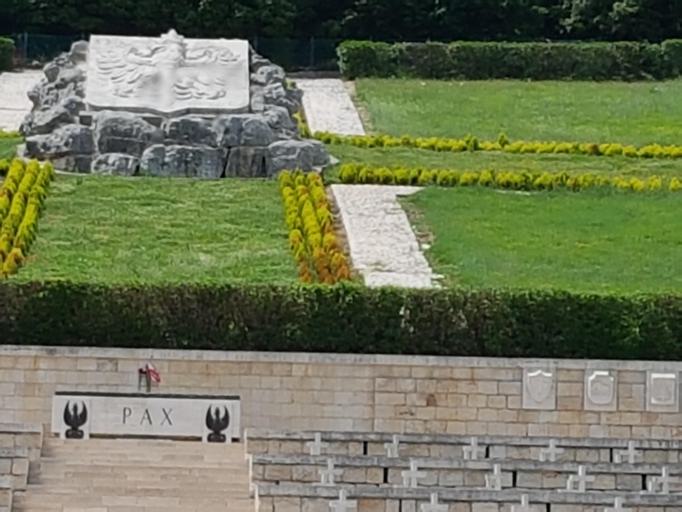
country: IT
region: Latium
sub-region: Provincia di Frosinone
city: Cassino
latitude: 41.4939
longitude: 13.8061
